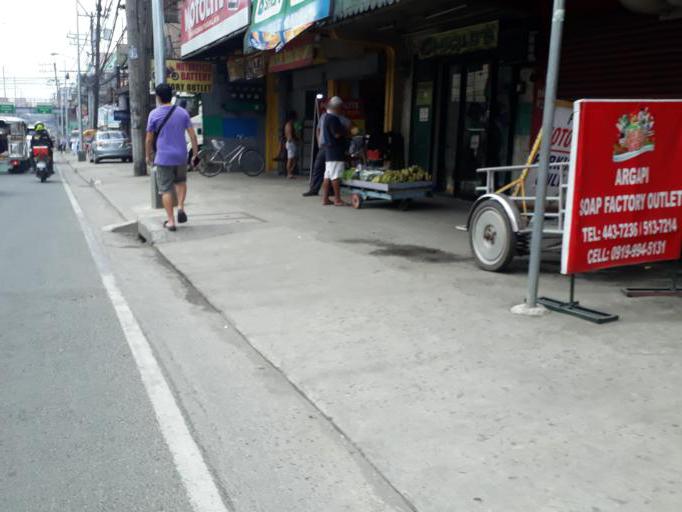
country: PH
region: Calabarzon
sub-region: Province of Rizal
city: Valenzuela
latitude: 14.6795
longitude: 120.9795
